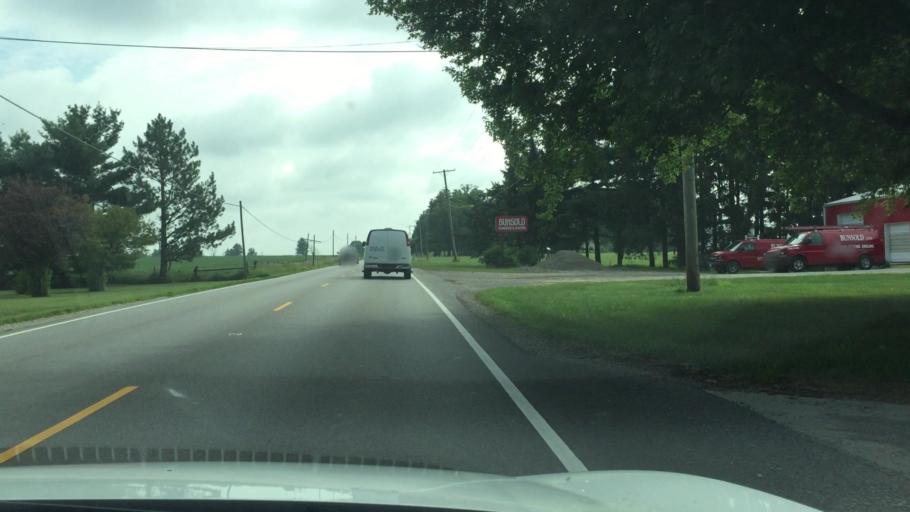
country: US
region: Ohio
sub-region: Union County
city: Marysville
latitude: 40.1944
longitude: -83.4165
